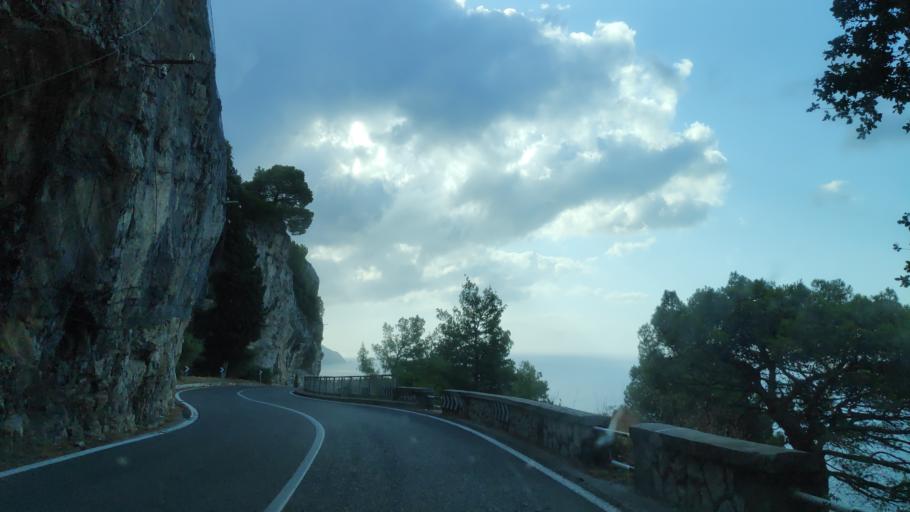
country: IT
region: Campania
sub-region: Provincia di Napoli
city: Arola-Preazzano
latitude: 40.6167
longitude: 14.4371
